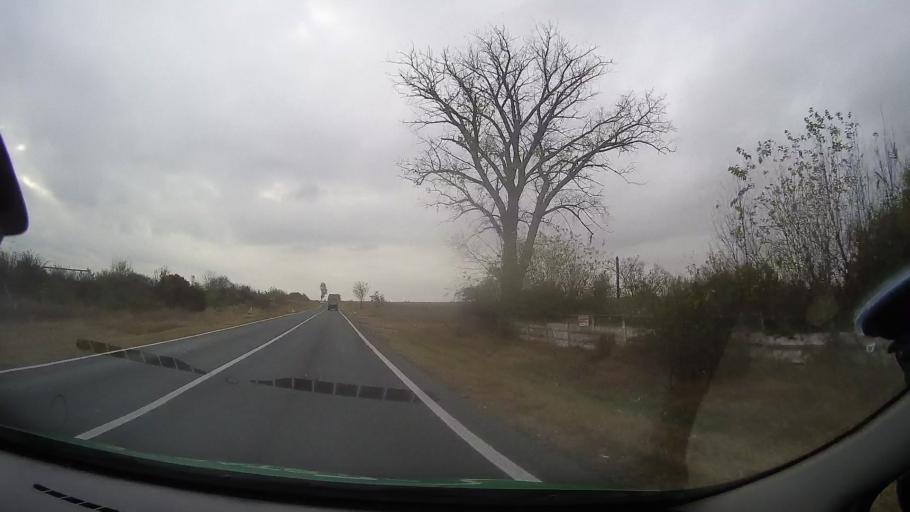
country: RO
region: Constanta
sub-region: Comuna Castelu
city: Castelu
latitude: 44.2533
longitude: 28.3218
